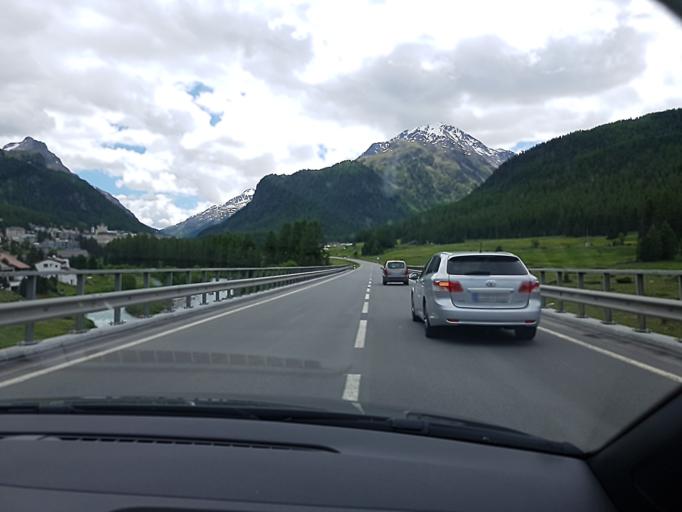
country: CH
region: Grisons
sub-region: Maloja District
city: Pontresina
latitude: 46.5024
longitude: 9.8880
